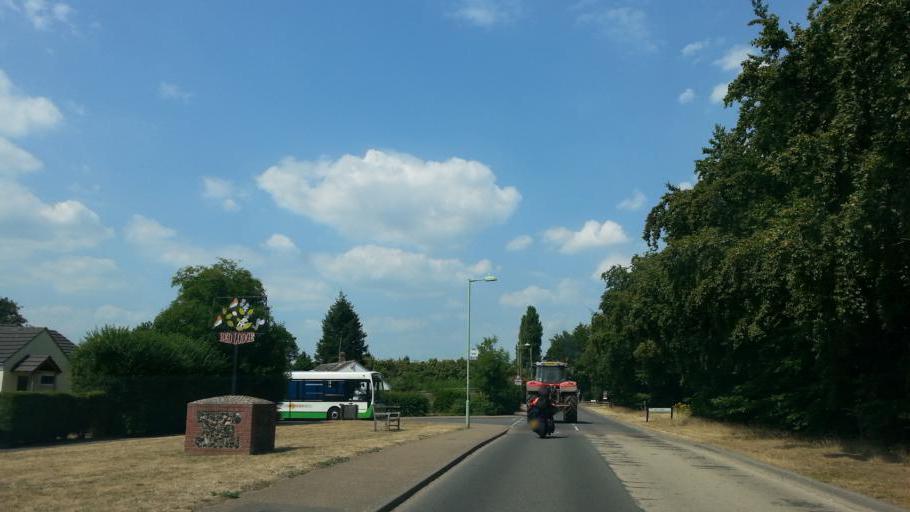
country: GB
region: England
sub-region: Cambridgeshire
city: Isleham
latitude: 52.3056
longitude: 0.4951
